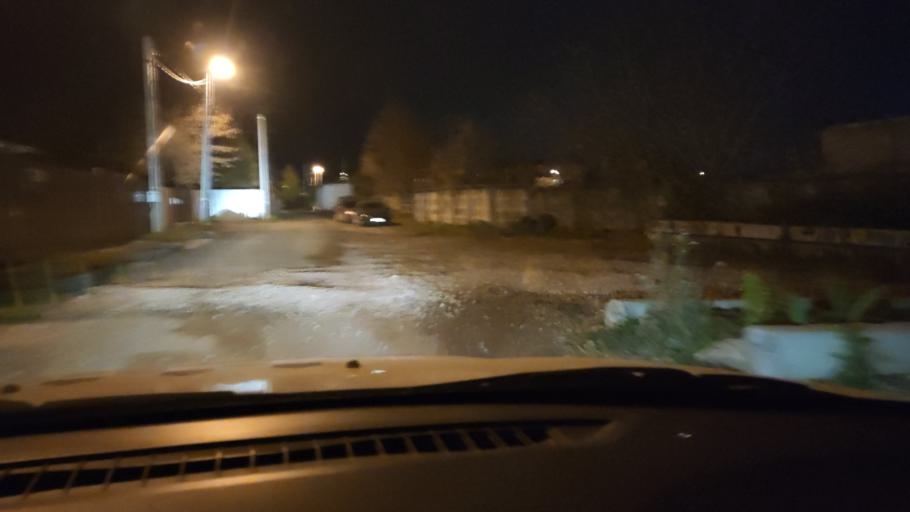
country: RU
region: Perm
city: Kondratovo
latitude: 57.9640
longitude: 56.1452
